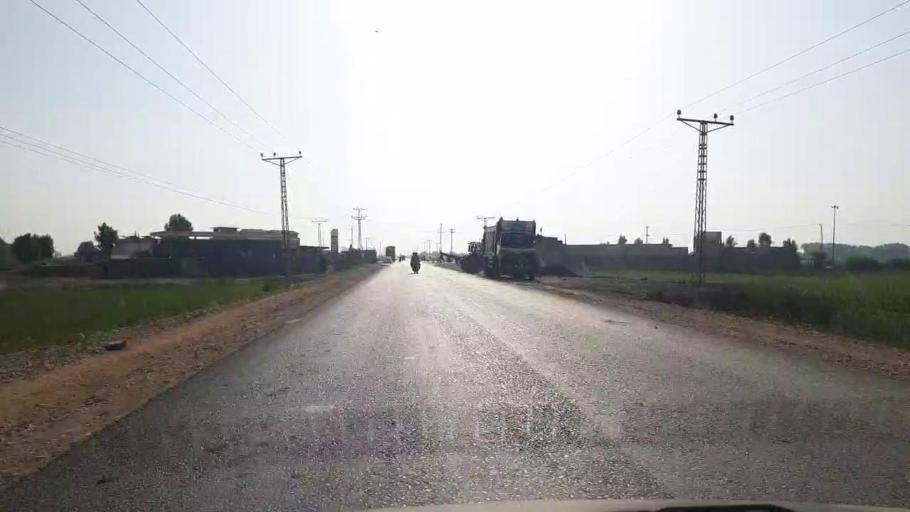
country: PK
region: Sindh
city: Badin
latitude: 24.6671
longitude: 68.8666
